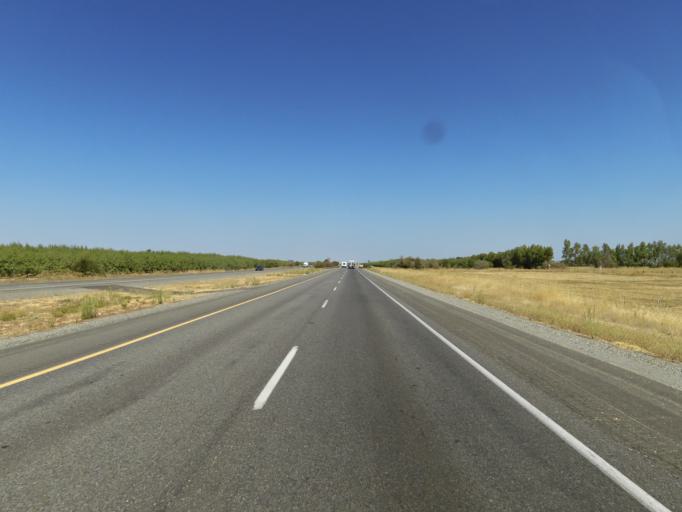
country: US
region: California
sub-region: Tehama County
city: Gerber
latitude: 40.0106
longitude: -122.2074
